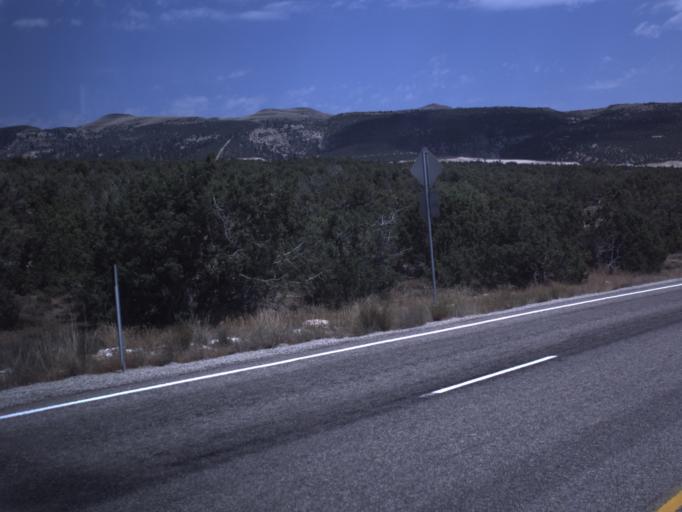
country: US
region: Utah
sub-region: Uintah County
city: Vernal
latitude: 40.6142
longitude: -109.4759
